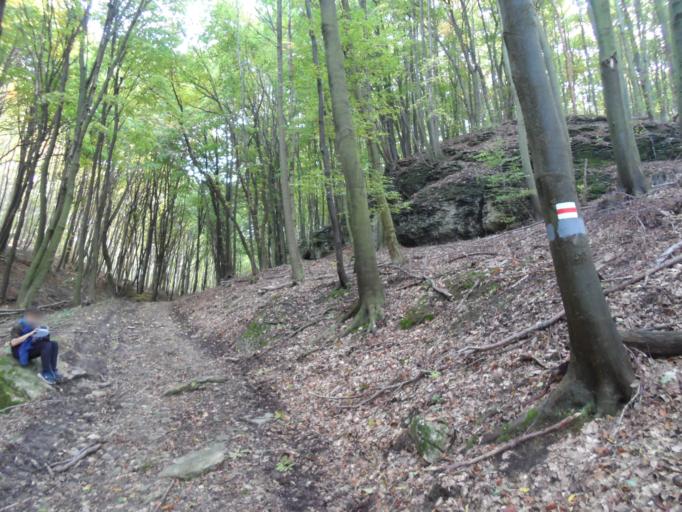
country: HU
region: Veszprem
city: Zirc
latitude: 47.3169
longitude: 17.9061
